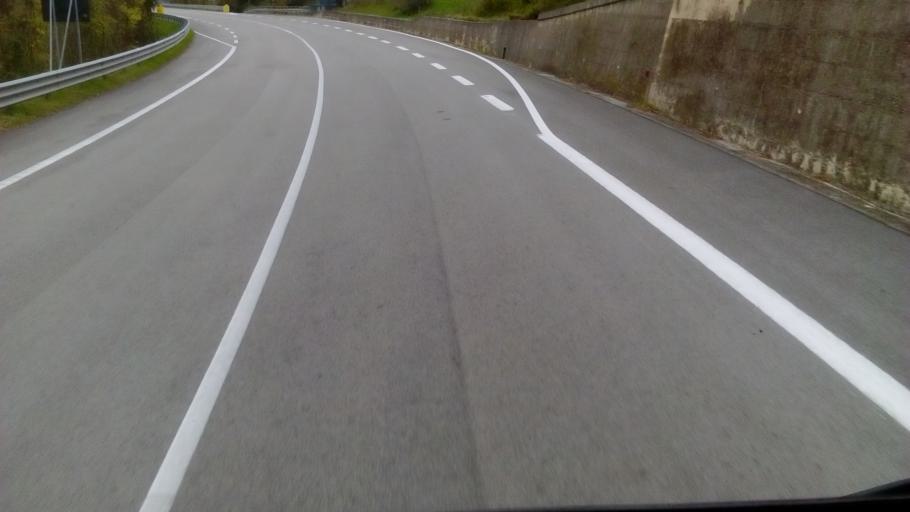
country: IT
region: Molise
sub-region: Provincia di Campobasso
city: Trivento
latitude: 41.7918
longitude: 14.5410
